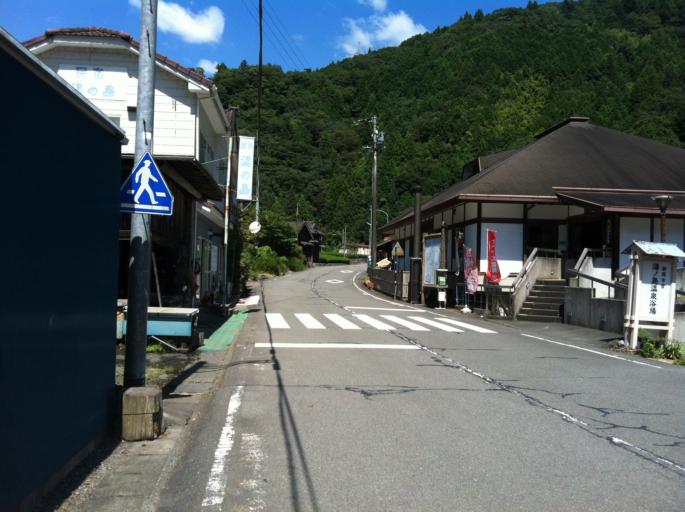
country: JP
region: Shizuoka
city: Shizuoka-shi
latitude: 35.1073
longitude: 138.2273
